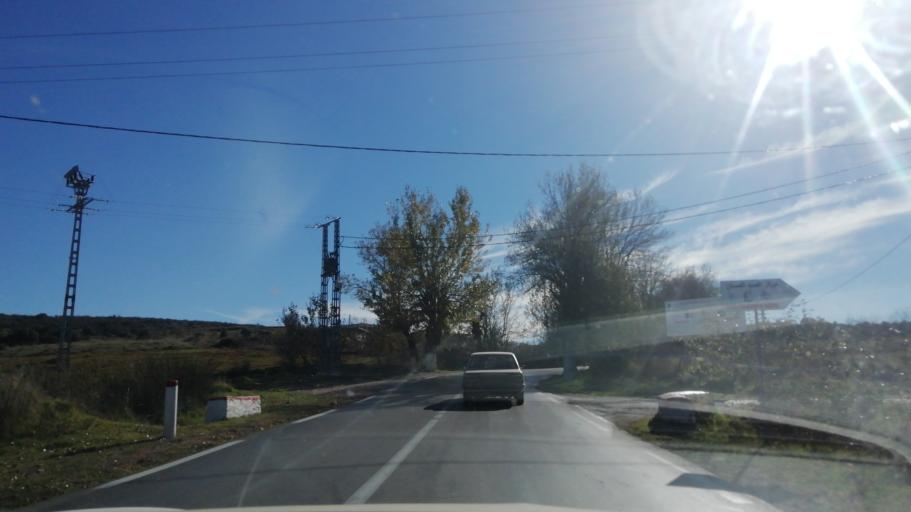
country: DZ
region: Tlemcen
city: Mansoura
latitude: 34.8365
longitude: -1.3725
